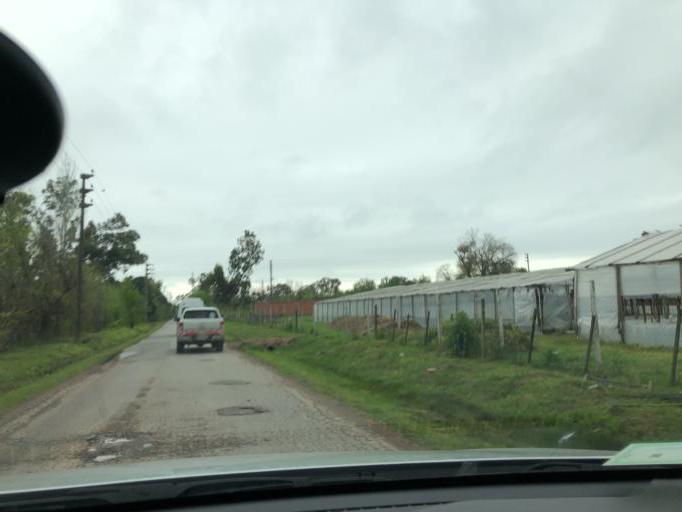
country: AR
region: Buenos Aires
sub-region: Partido de La Plata
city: La Plata
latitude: -34.9007
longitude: -58.0913
